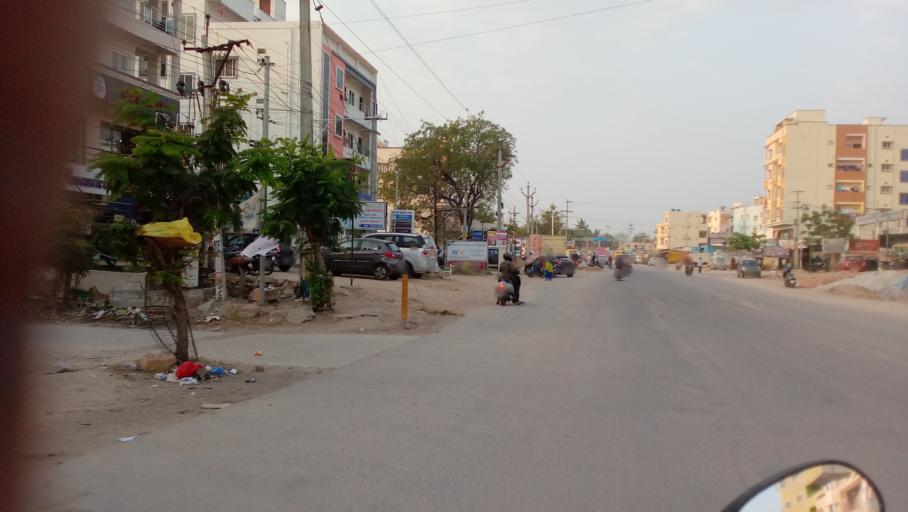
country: IN
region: Telangana
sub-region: Medak
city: Serilingampalle
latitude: 17.5069
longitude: 78.3183
